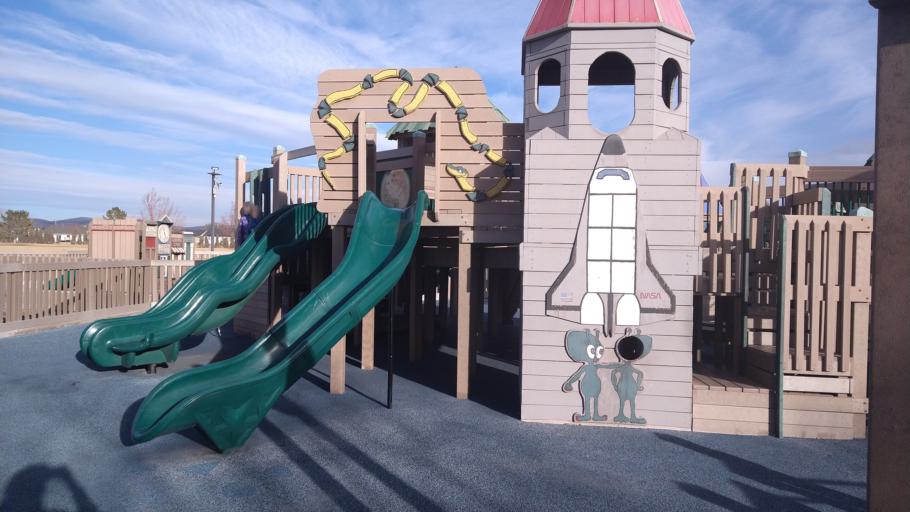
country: US
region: Idaho
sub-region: Bannock County
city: Chubbuck
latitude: 42.9075
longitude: -112.4833
